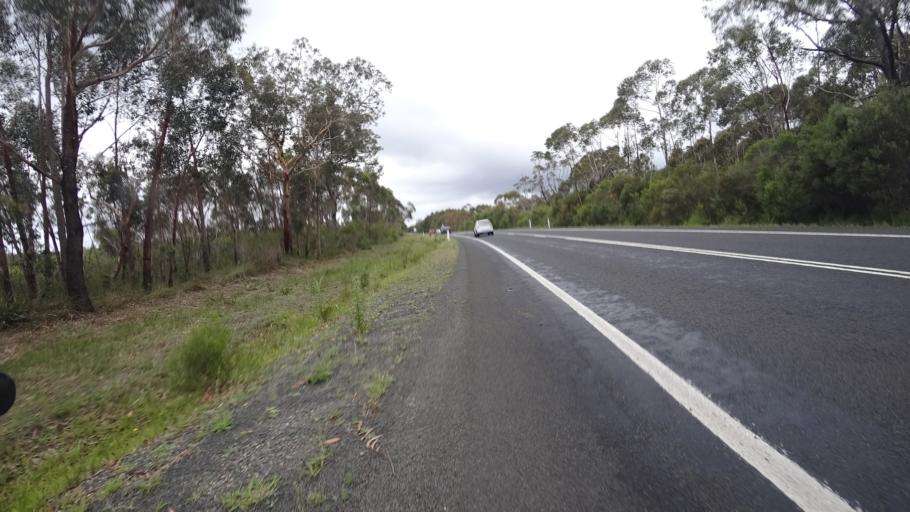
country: AU
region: New South Wales
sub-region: Shoalhaven Shire
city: Milton
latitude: -35.1097
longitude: 150.3408
